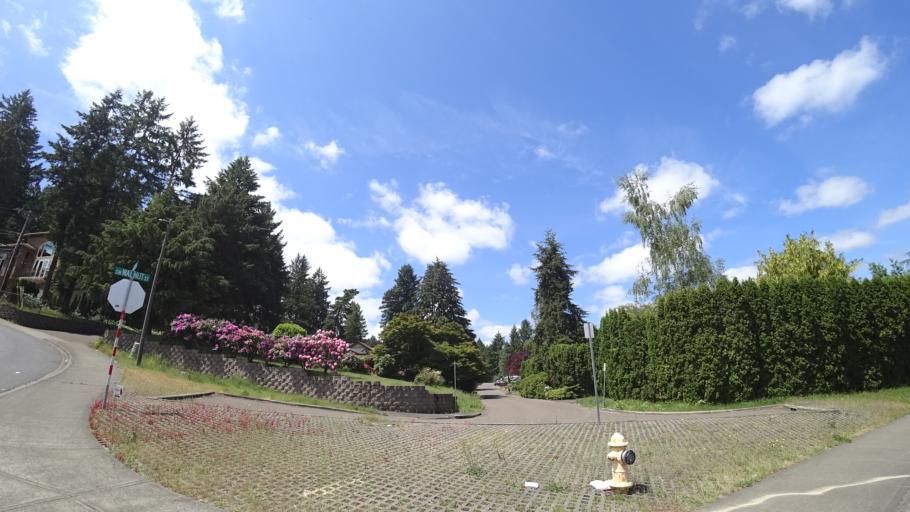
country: US
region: Oregon
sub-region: Washington County
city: King City
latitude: 45.4291
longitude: -122.8157
